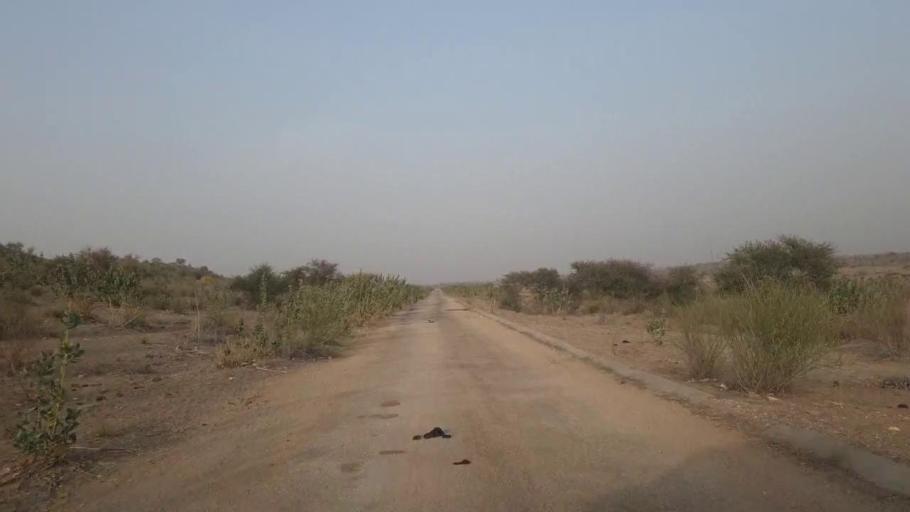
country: PK
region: Sindh
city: Chor
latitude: 25.4970
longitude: 69.9264
